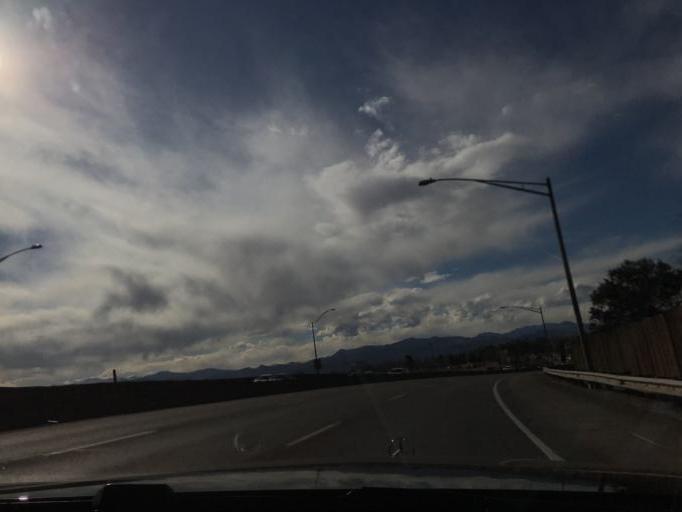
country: US
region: Colorado
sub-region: Adams County
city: Berkley
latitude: 39.7836
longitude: -105.0438
